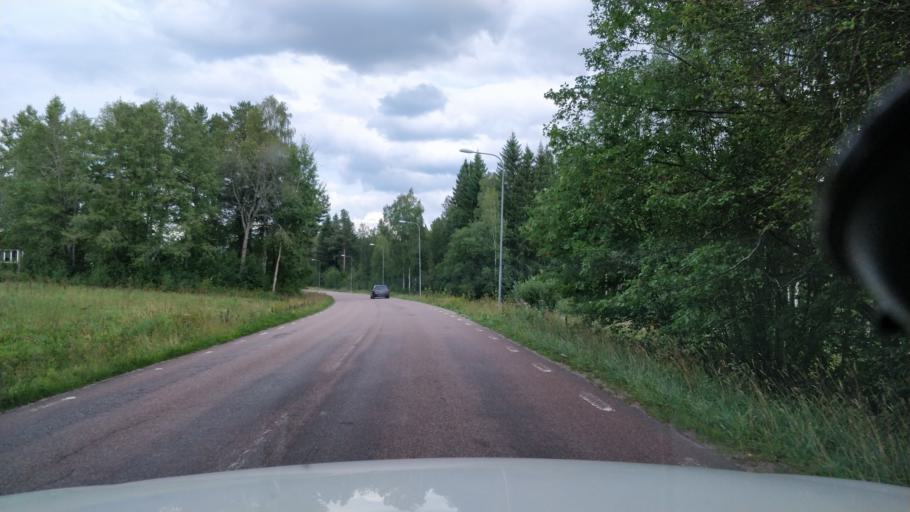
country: SE
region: Dalarna
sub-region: Faluns Kommun
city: Bjursas
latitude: 60.7418
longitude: 15.4677
